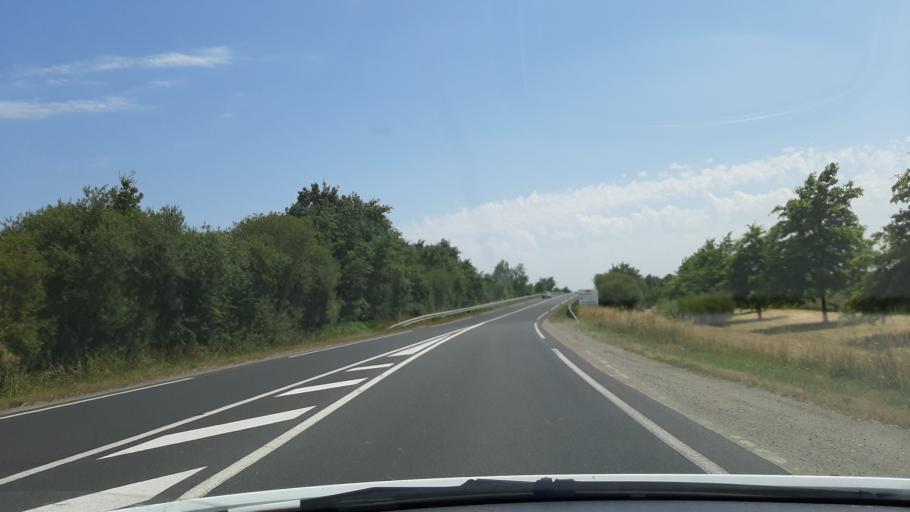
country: FR
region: Pays de la Loire
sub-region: Departement de la Vendee
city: Mouilleron-le-Captif
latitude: 46.7443
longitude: -1.4390
